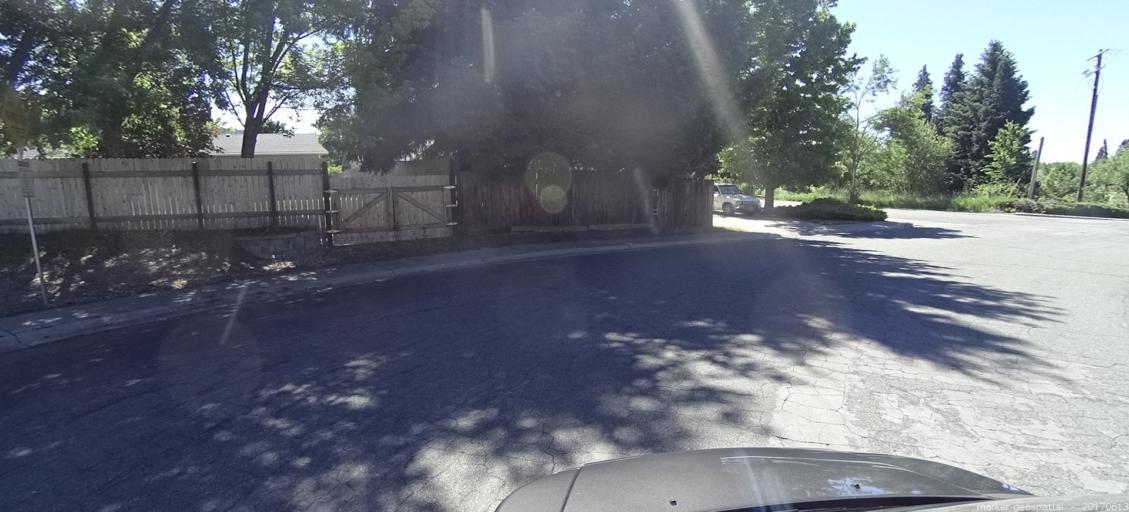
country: US
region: California
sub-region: Siskiyou County
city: Mount Shasta
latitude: 41.3201
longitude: -122.3135
